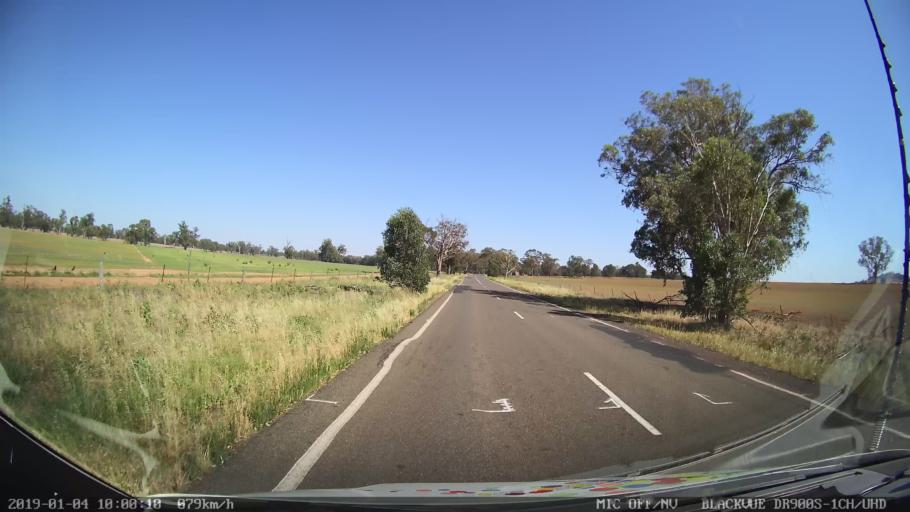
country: AU
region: New South Wales
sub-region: Cabonne
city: Canowindra
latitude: -33.5003
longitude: 148.3808
